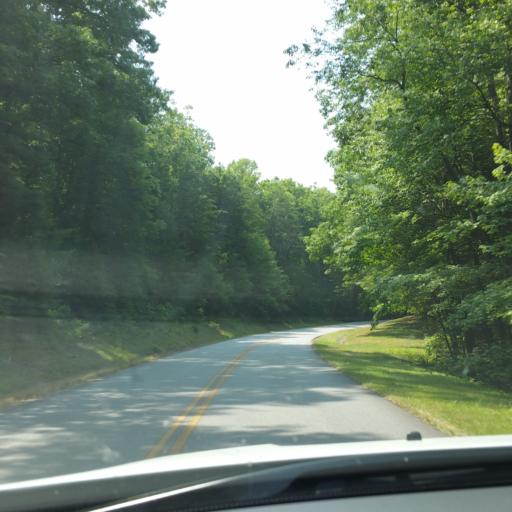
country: US
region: North Carolina
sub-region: Buncombe County
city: Avery Creek
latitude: 35.5005
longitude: -82.5580
